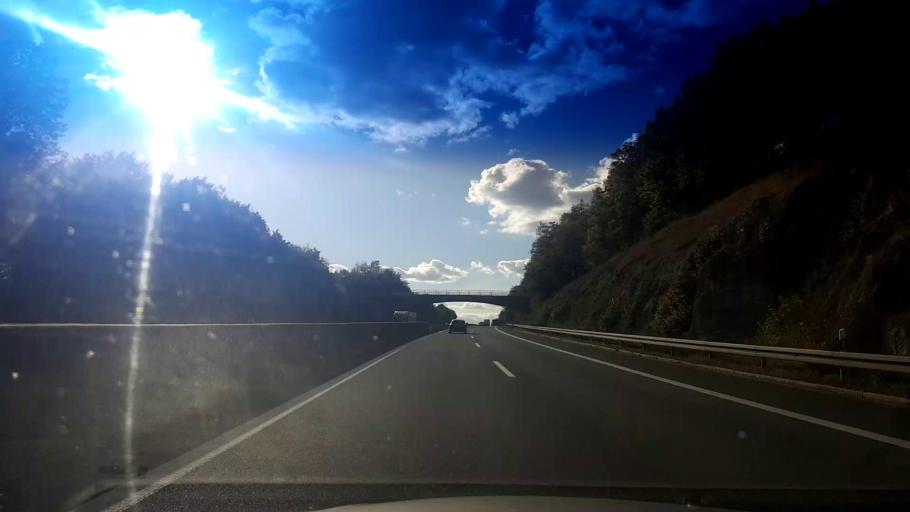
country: DE
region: Bavaria
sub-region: Upper Franconia
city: Kasendorf
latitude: 50.0091
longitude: 11.3597
